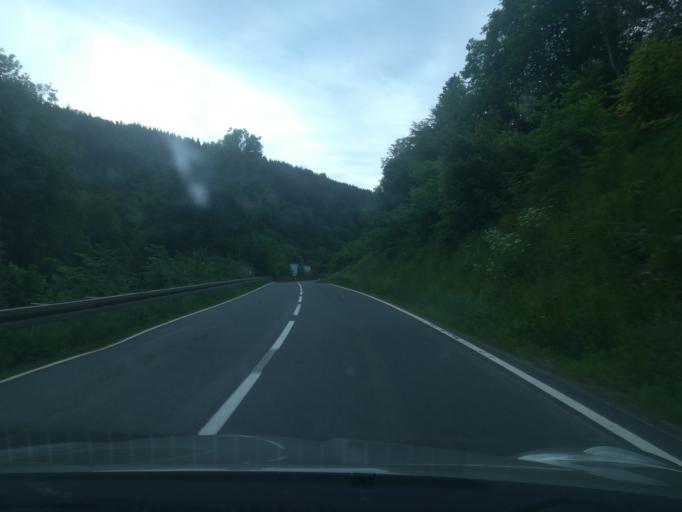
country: DE
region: Saxony-Anhalt
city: Rubeland
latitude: 51.7578
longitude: 10.8616
